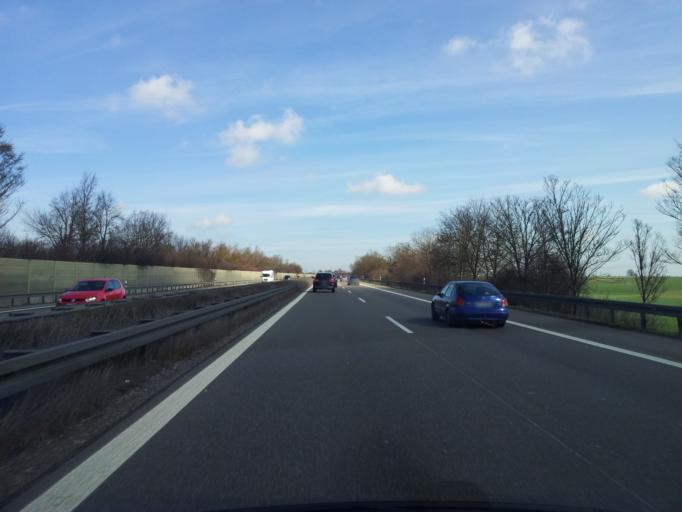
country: DE
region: Baden-Wuerttemberg
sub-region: Regierungsbezirk Stuttgart
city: Motzingen
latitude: 48.4673
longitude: 8.7857
